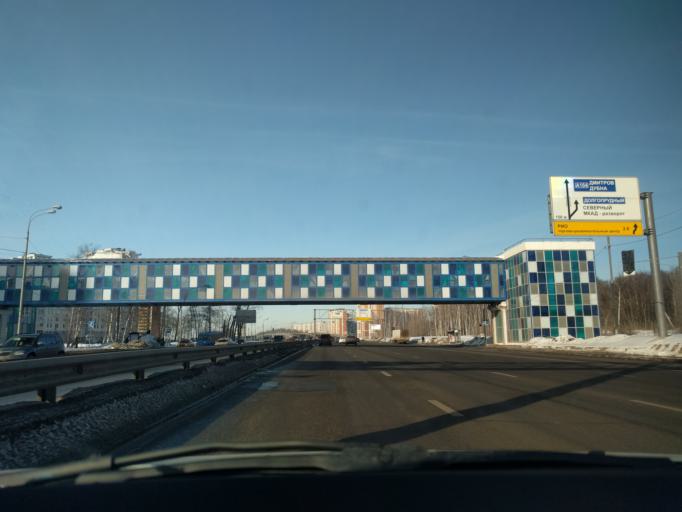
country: RU
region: Moscow
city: Severnyy
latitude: 55.9252
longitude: 37.5463
